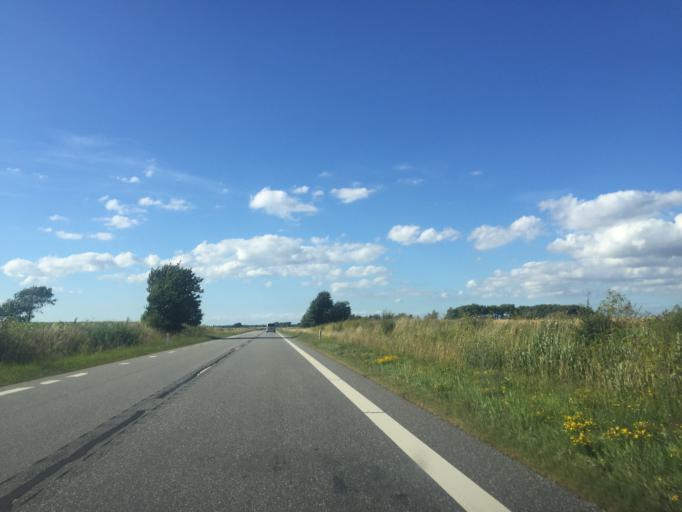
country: DK
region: Zealand
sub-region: Guldborgsund Kommune
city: Nykobing Falster
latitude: 54.6145
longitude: 11.9284
